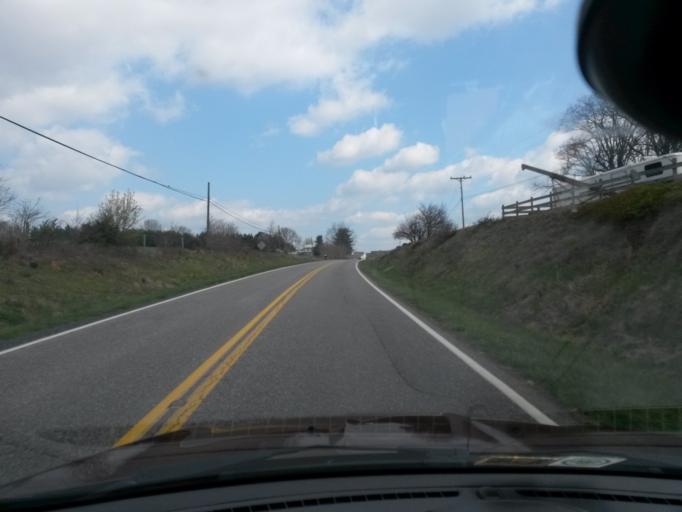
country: US
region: Virginia
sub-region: Rockingham County
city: Massanetta Springs
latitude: 38.3835
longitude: -78.8167
